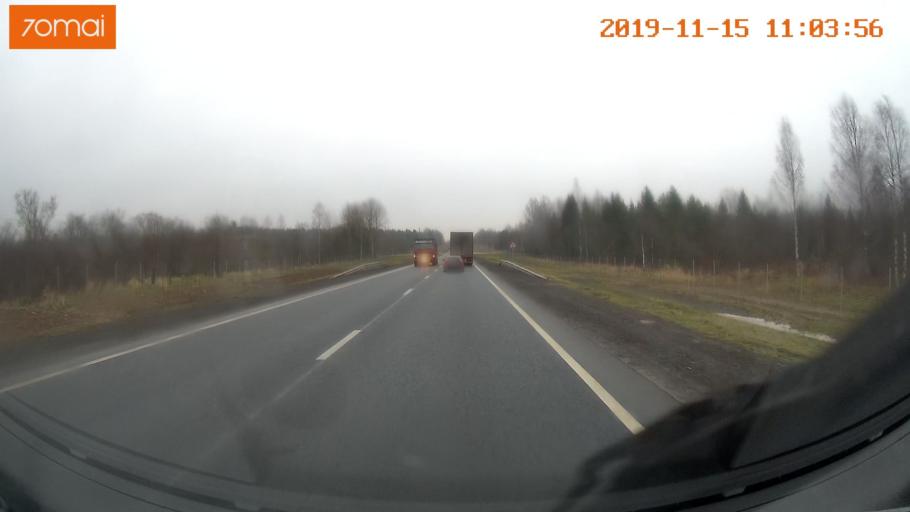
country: RU
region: Vologda
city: Chebsara
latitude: 59.1223
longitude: 38.9731
